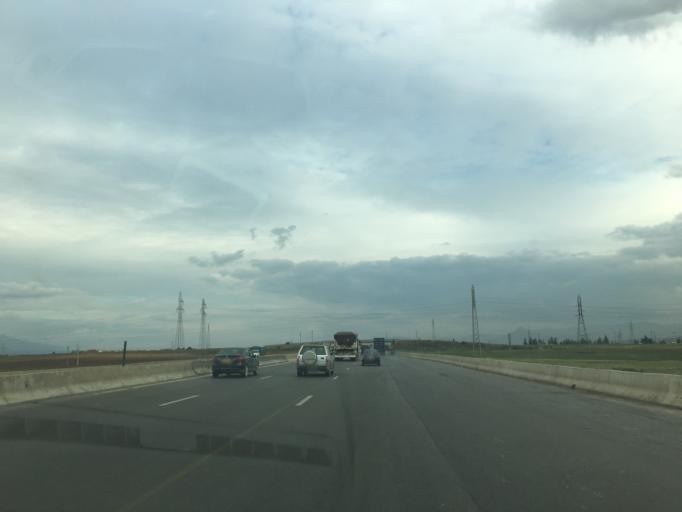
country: DZ
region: Bouira
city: Bouira
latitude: 36.3299
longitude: 3.9455
